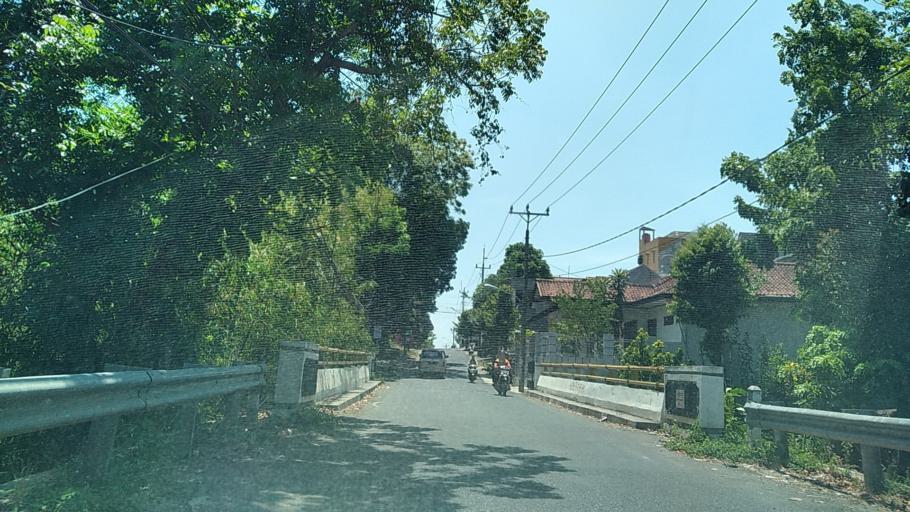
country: ID
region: Central Java
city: Ungaran
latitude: -7.0911
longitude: 110.4148
